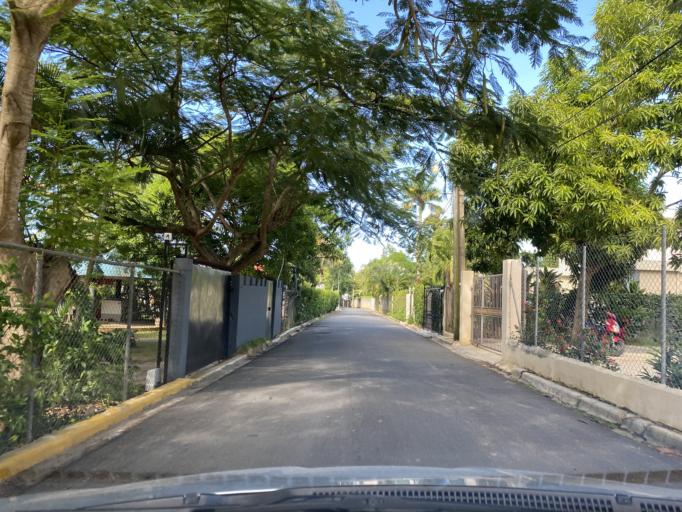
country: DO
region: Samana
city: Las Terrenas
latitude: 19.3055
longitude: -69.5449
